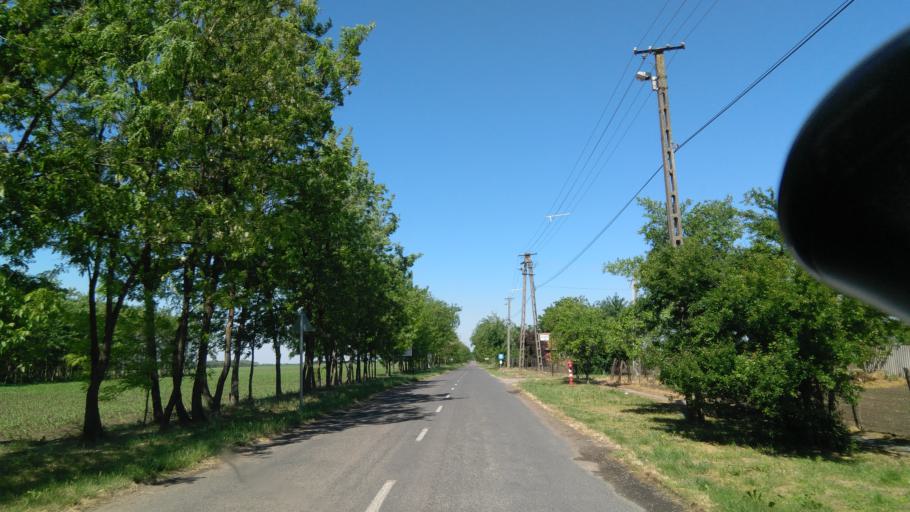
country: HU
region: Bekes
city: Kunagota
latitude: 46.4228
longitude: 21.1124
